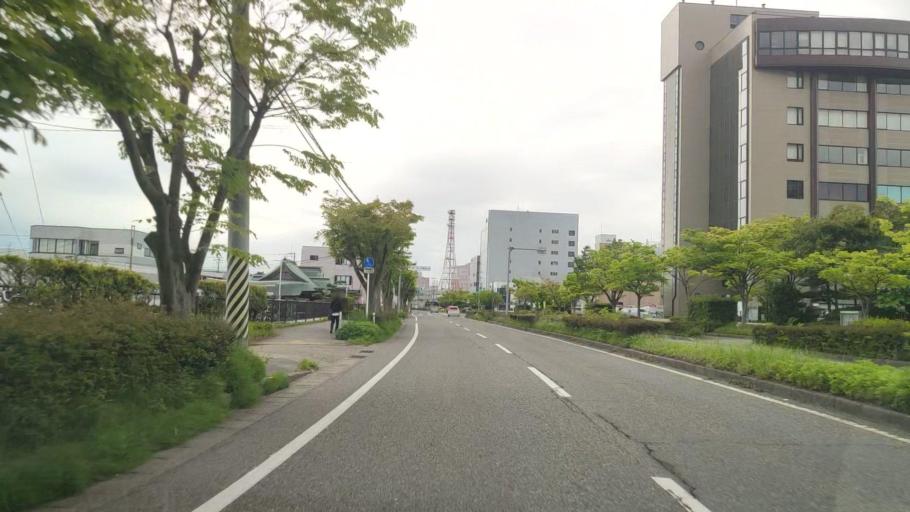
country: JP
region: Niigata
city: Niigata-shi
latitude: 37.9005
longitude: 139.0234
